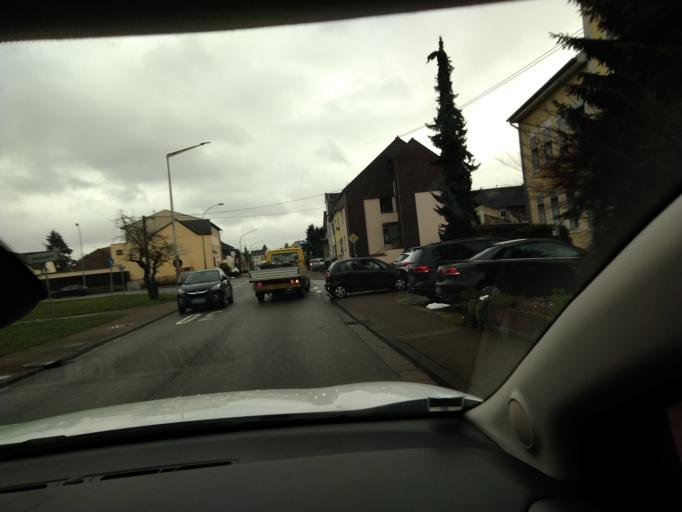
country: DE
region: Saarland
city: Saarlouis
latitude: 49.3285
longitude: 6.7612
